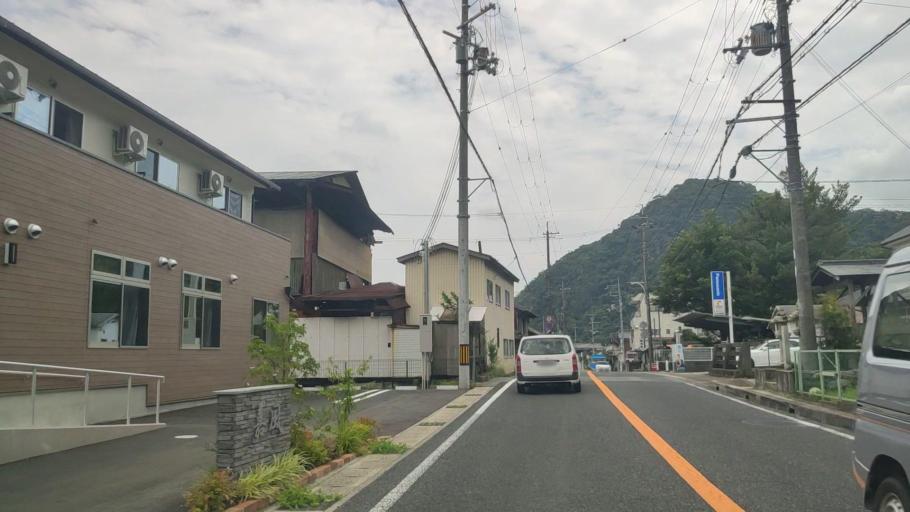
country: JP
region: Hyogo
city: Tatsunocho-tominaga
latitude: 34.8799
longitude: 134.5462
